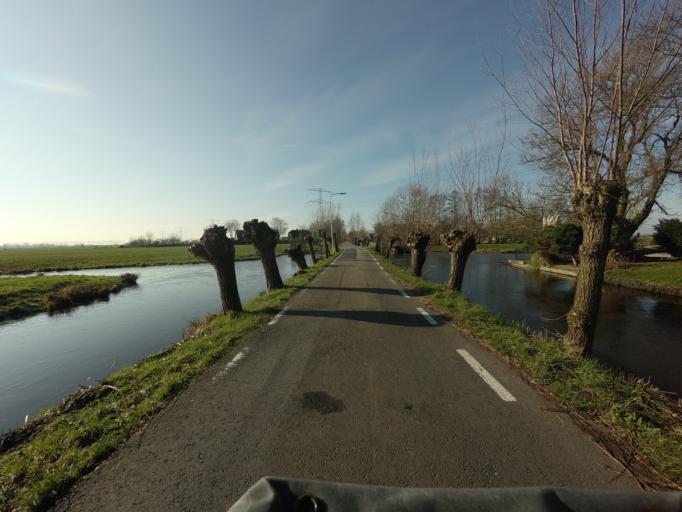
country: NL
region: Utrecht
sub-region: Gemeente Oudewater
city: Oudewater
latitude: 52.0285
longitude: 4.8243
